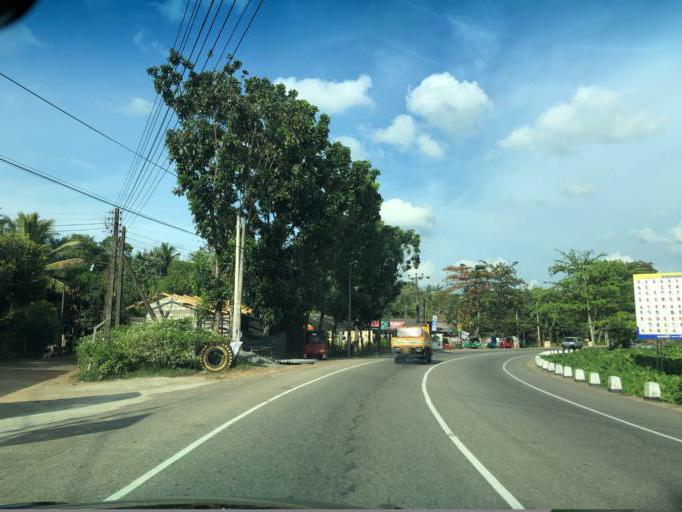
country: LK
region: Western
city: Horawala Junction
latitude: 6.5276
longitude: 80.0962
